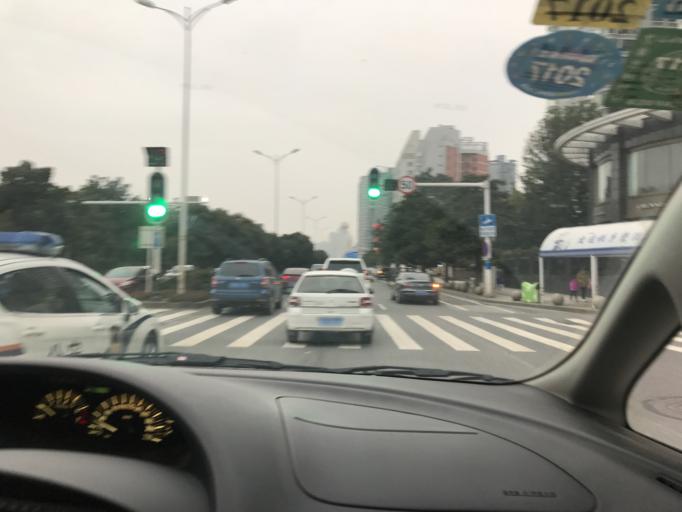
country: CN
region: Hubei
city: Jiang'an
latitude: 30.6083
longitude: 114.3081
